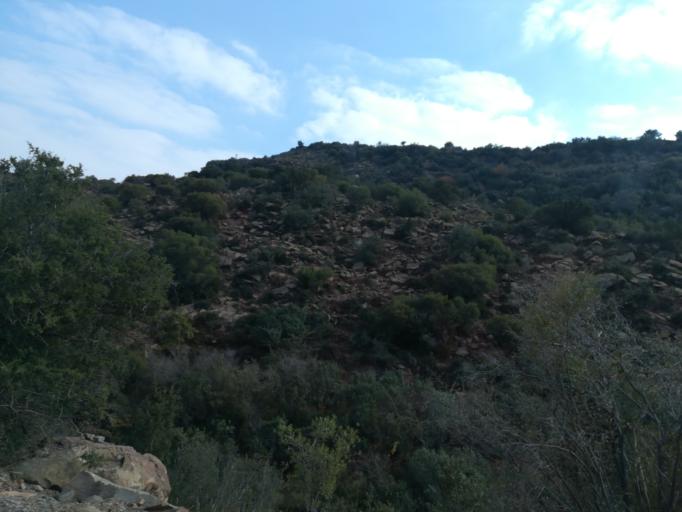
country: LS
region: Quthing
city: Quthing
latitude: -30.3366
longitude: 27.5456
